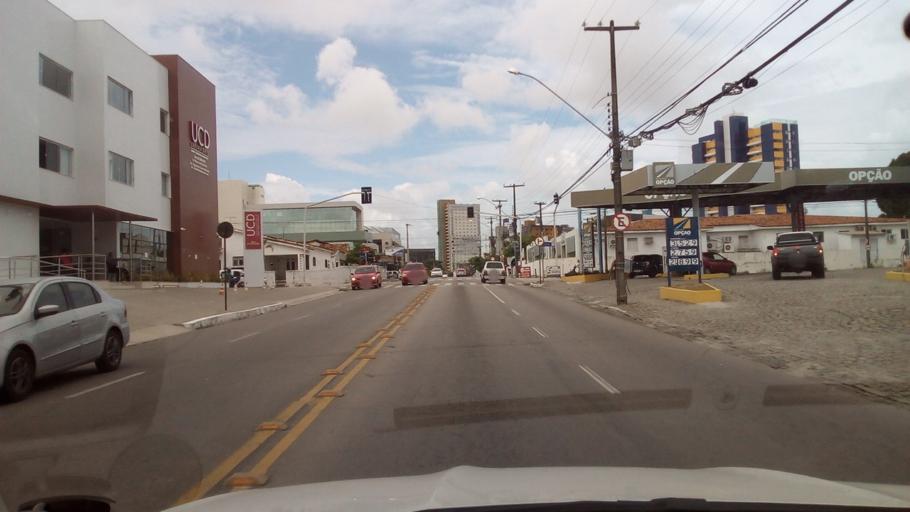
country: BR
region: Paraiba
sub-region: Joao Pessoa
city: Joao Pessoa
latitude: -7.1244
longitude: -34.8595
